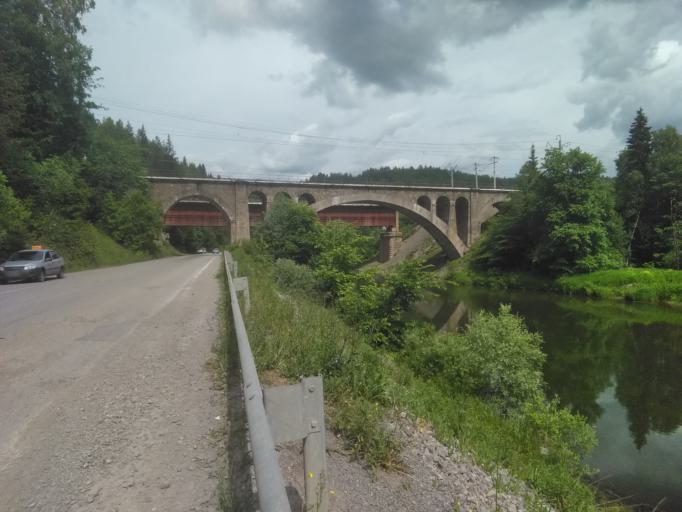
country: RU
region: Chelyabinsk
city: Sim
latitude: 55.0675
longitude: 57.6097
